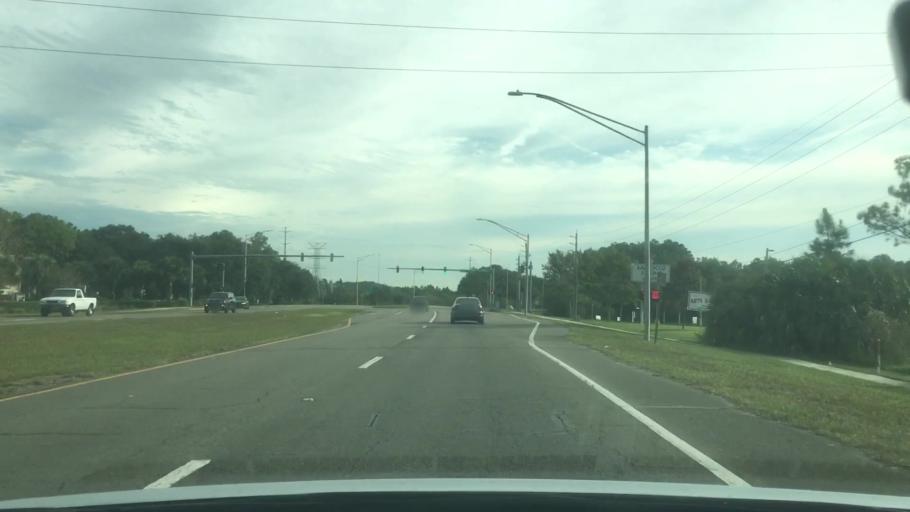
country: US
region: Florida
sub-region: Duval County
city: Neptune Beach
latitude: 30.2787
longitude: -81.5245
